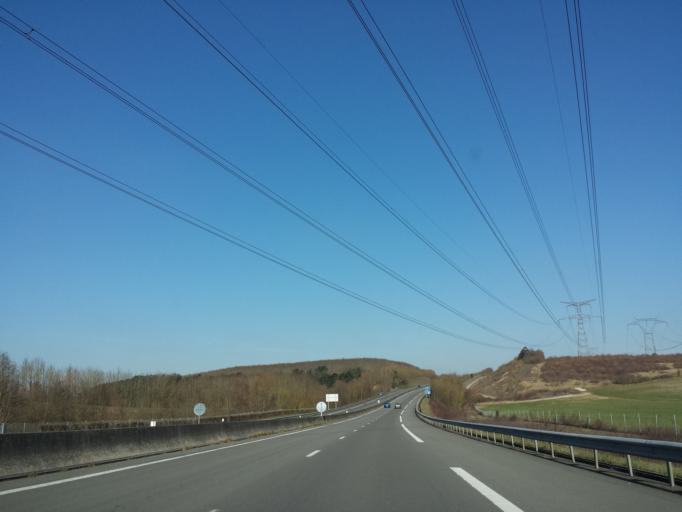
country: FR
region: Picardie
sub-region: Departement de la Somme
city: Conty
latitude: 49.7457
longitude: 2.2309
